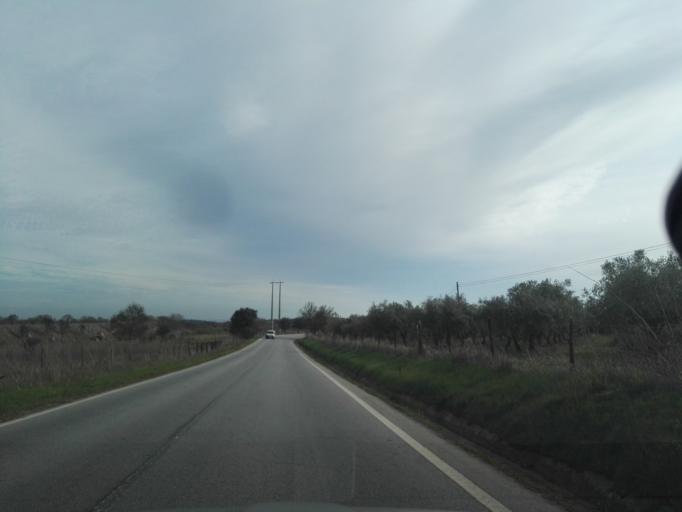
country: PT
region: Portalegre
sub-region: Elvas
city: Elvas
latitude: 38.9314
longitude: -7.1843
